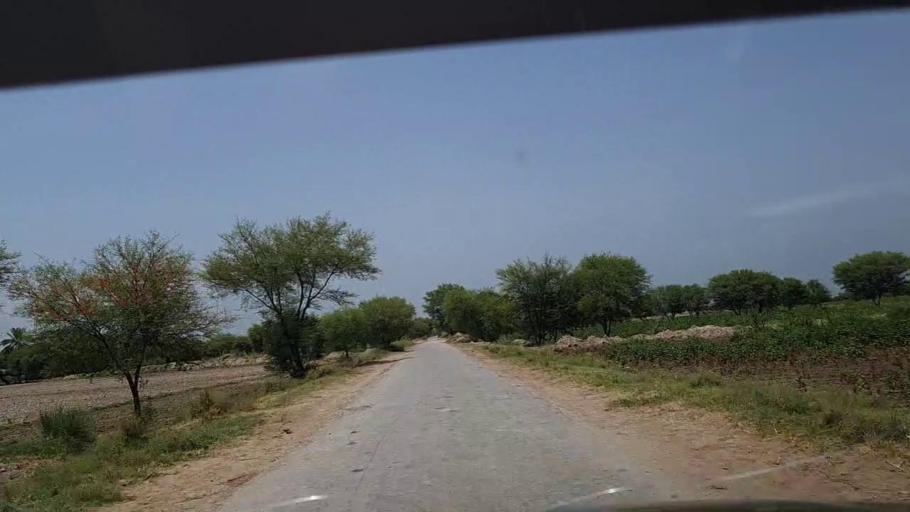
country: PK
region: Sindh
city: Khanpur
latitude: 27.7951
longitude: 69.4543
